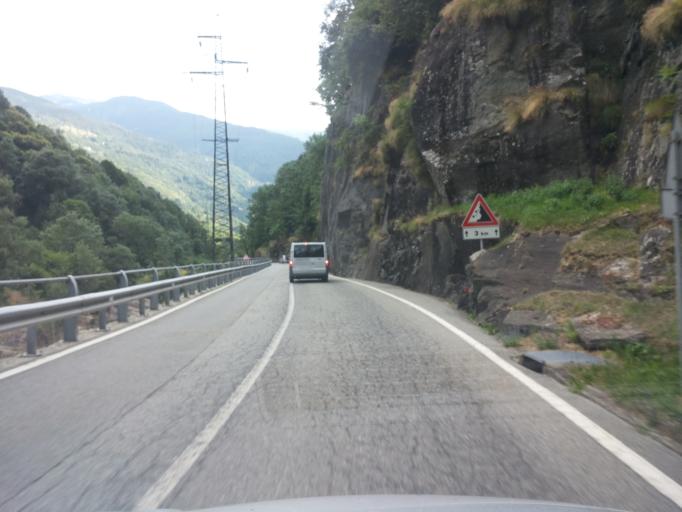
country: IT
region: Aosta Valley
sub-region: Valle d'Aosta
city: Issime
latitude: 45.6688
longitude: 7.8584
